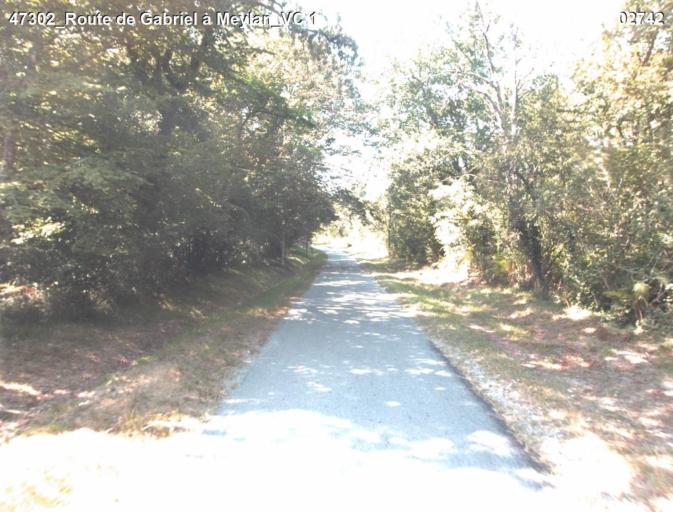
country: FR
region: Aquitaine
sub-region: Departement du Lot-et-Garonne
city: Mezin
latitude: 44.0717
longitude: 0.1302
